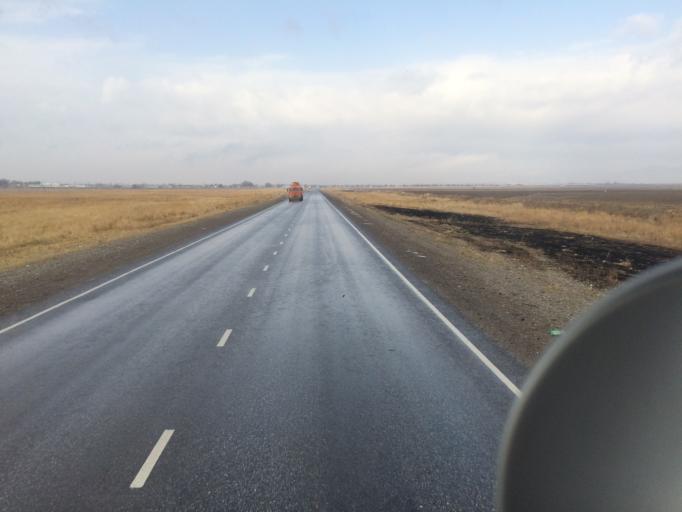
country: KZ
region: Zhambyl
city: Georgiyevka
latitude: 43.0801
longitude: 74.7220
